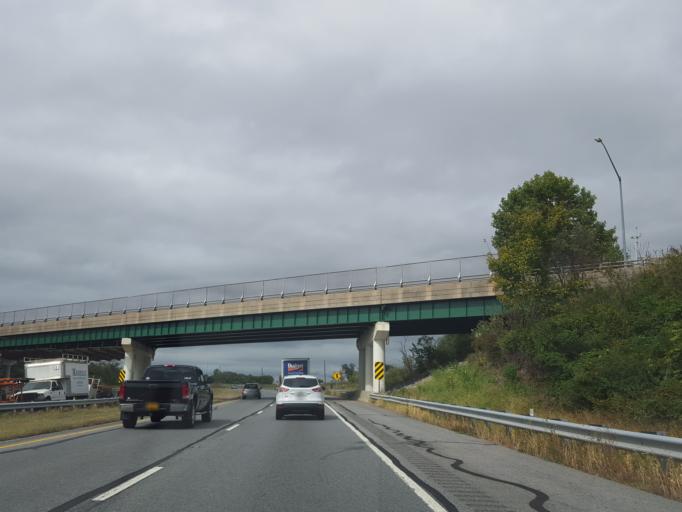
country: US
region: Maryland
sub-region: Frederick County
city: Jefferson
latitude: 39.3558
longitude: -77.5818
